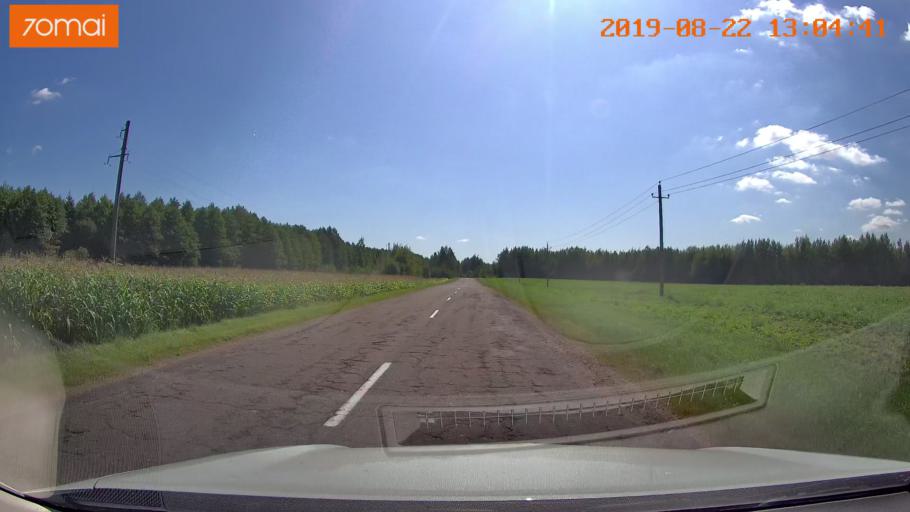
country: BY
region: Minsk
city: Prawdzinski
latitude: 53.3676
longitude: 27.8275
